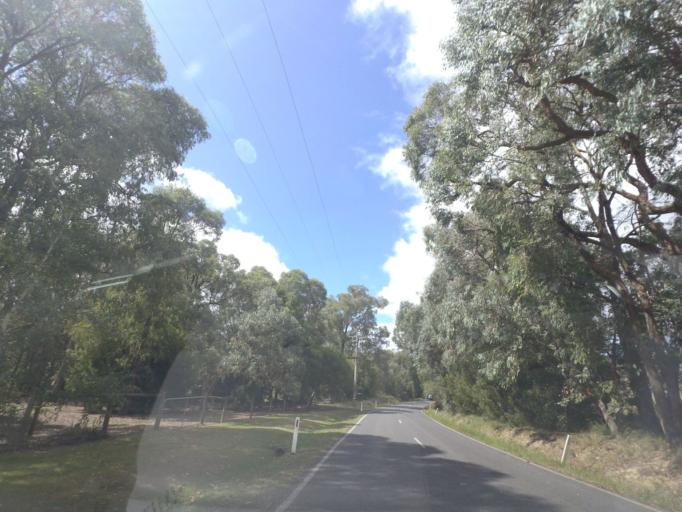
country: AU
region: Victoria
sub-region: Yarra Ranges
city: Launching Place
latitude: -37.7924
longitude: 145.5744
